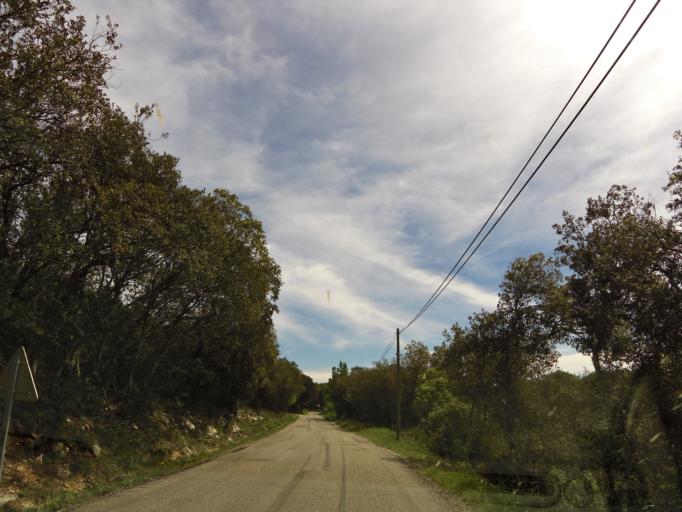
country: FR
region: Languedoc-Roussillon
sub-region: Departement du Gard
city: Quissac
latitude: 43.8744
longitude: 4.0383
